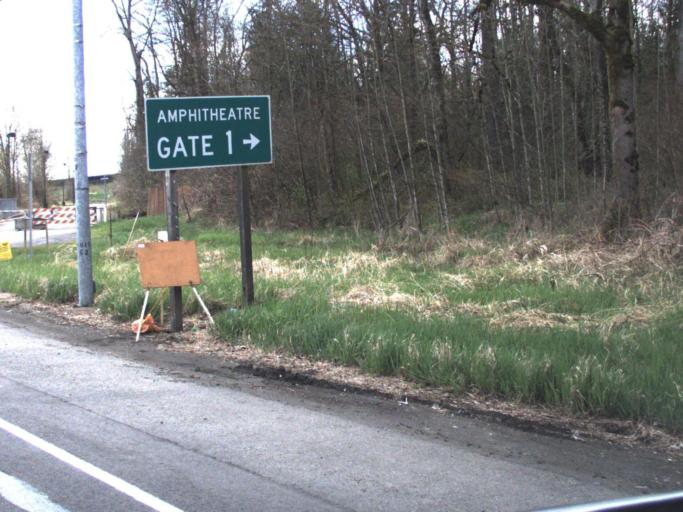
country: US
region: Washington
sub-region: King County
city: Lake Morton-Berrydale
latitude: 47.2431
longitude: -122.1122
